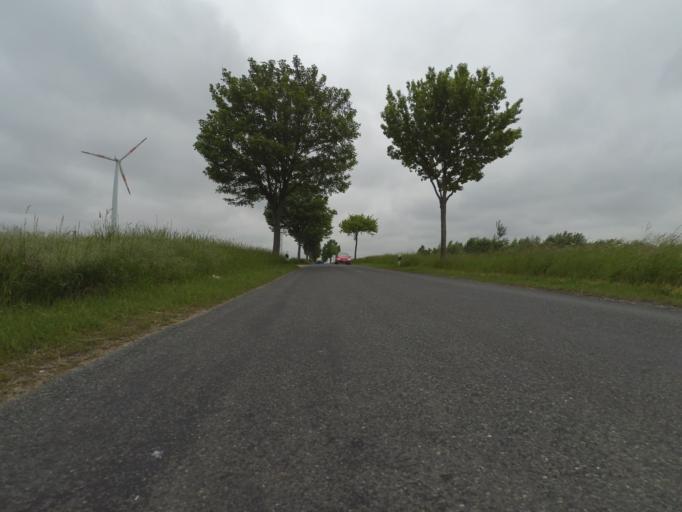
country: DE
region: Lower Saxony
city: Edemissen
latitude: 52.3516
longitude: 10.3076
